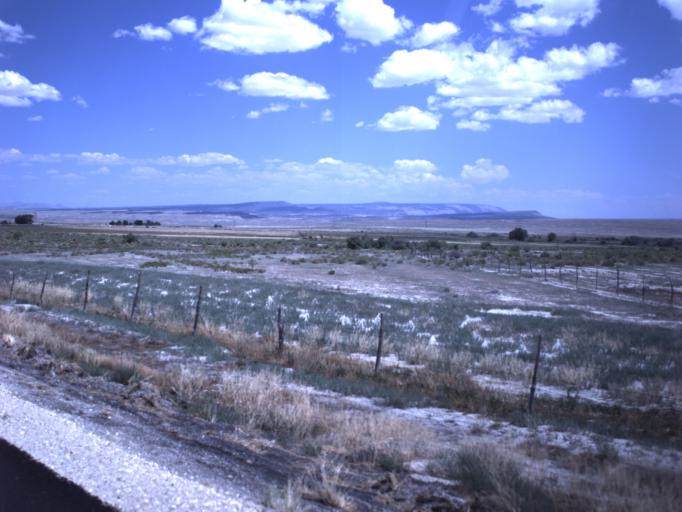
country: US
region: Utah
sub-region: Emery County
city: Castle Dale
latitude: 39.2373
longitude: -111.0052
